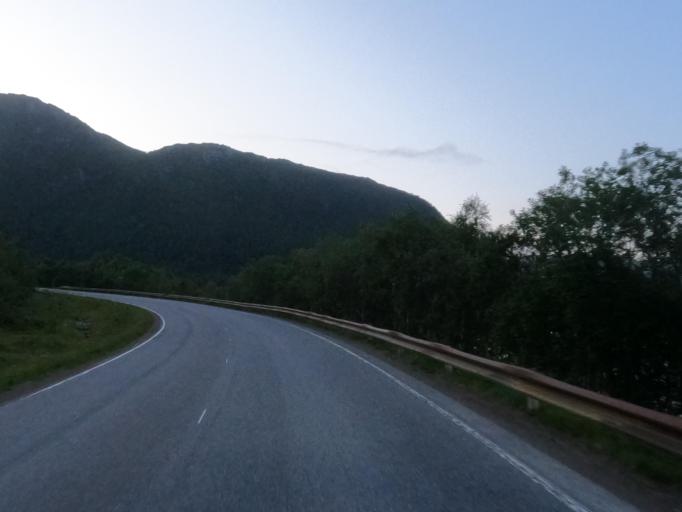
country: NO
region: Nordland
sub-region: Lodingen
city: Lodingen
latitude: 68.5526
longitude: 15.7514
